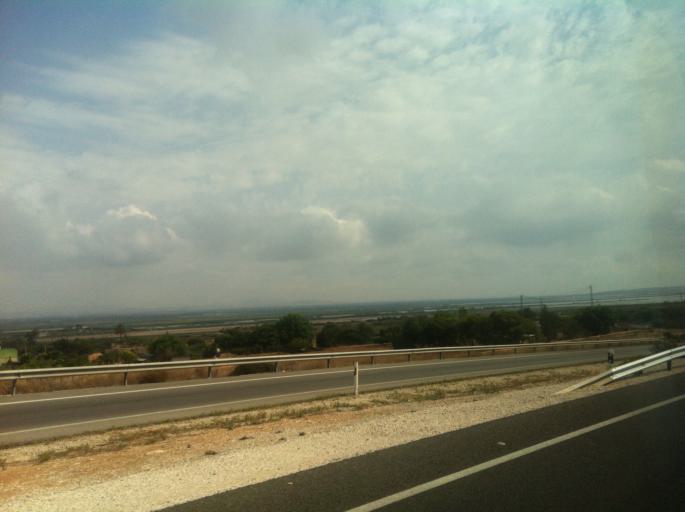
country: ES
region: Valencia
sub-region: Provincia de Alicante
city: Guardamar del Segura
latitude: 38.1583
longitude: -0.6536
